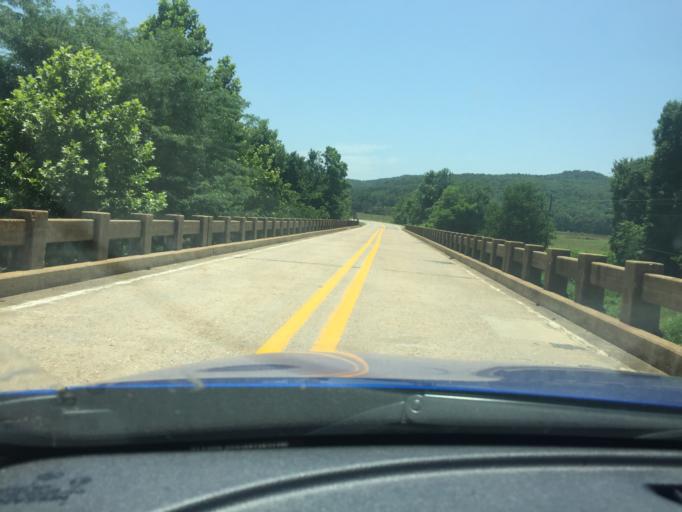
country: US
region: Arkansas
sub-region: Crawford County
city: Cedarville
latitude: 35.6458
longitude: -94.3936
